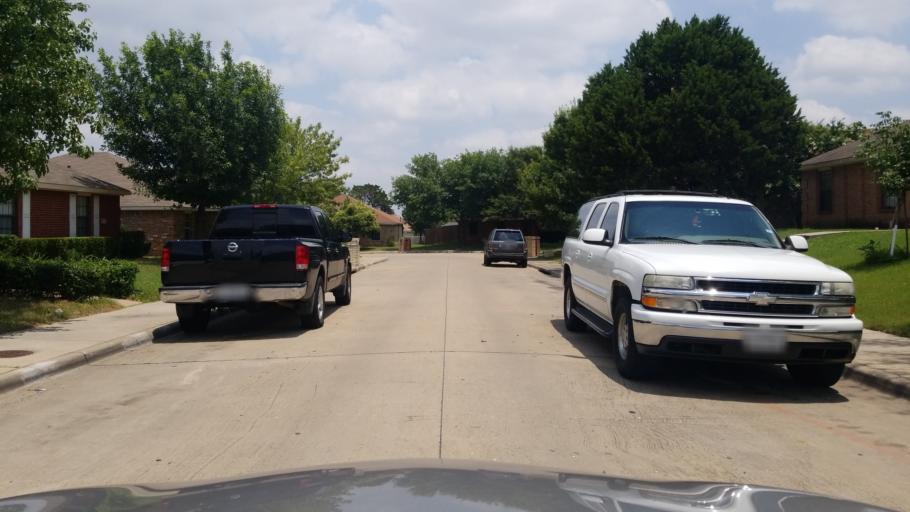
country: US
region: Texas
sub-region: Dallas County
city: Duncanville
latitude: 32.6841
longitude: -96.9107
